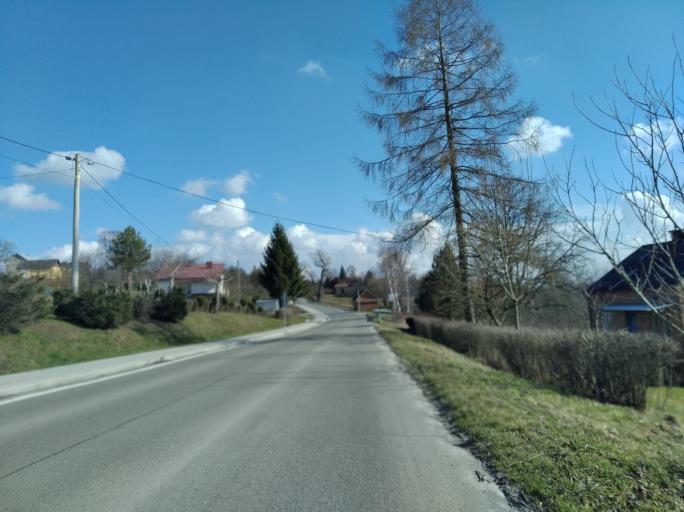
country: PL
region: Subcarpathian Voivodeship
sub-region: Powiat strzyzowski
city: Frysztak
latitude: 49.8443
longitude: 21.5812
